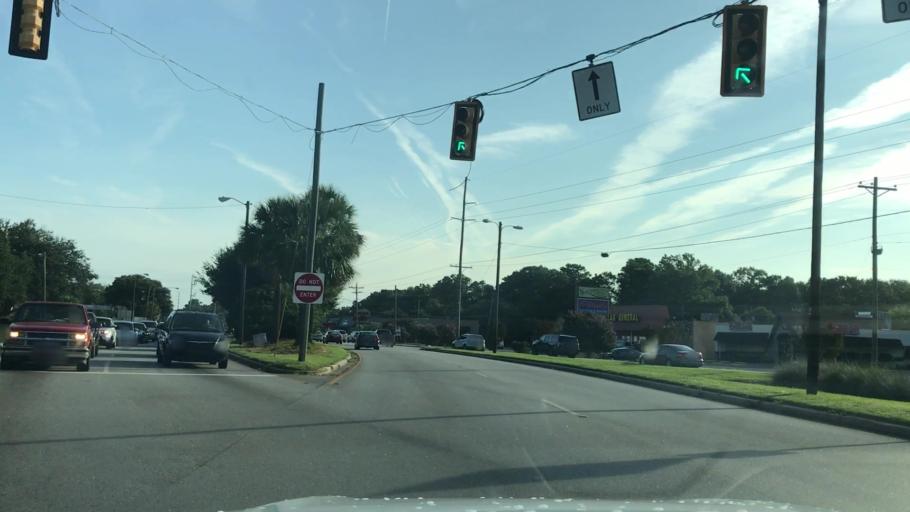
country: US
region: South Carolina
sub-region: Charleston County
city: North Charleston
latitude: 32.8174
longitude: -79.9934
